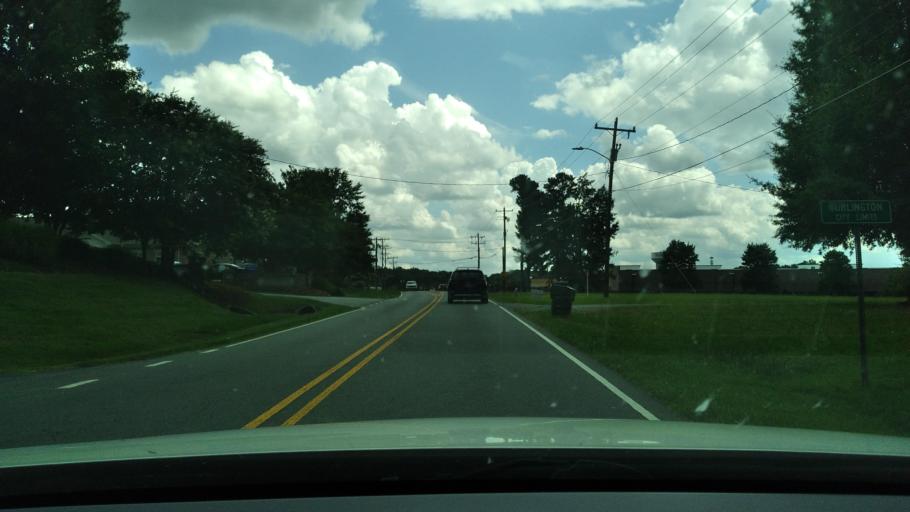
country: US
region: North Carolina
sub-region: Alamance County
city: Elon
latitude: 36.0827
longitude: -79.5170
